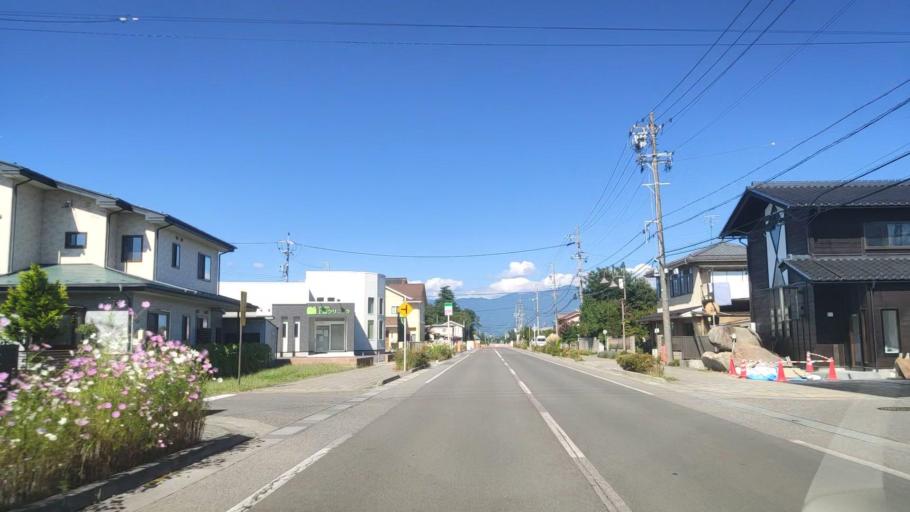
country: JP
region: Nagano
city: Shiojiri
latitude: 36.1490
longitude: 137.9444
